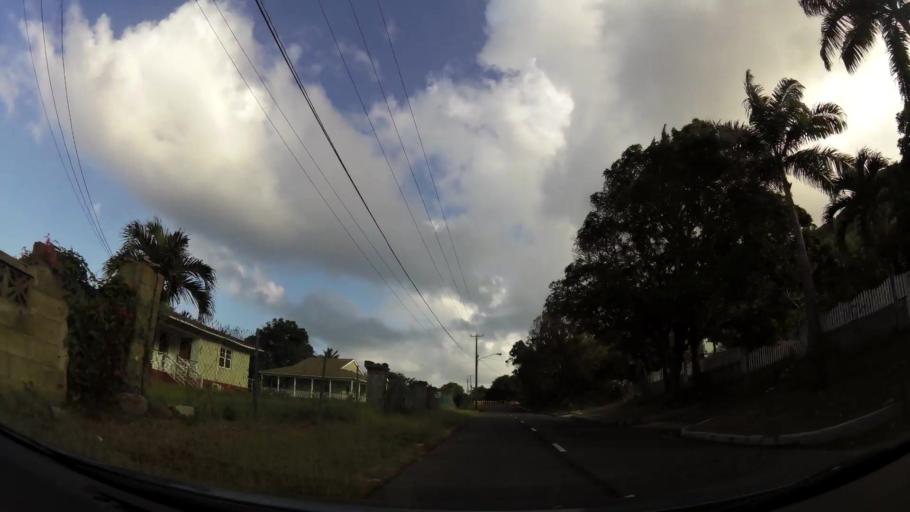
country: KN
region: Saint James Windwa
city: Newcastle
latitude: 17.1927
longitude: -62.5670
